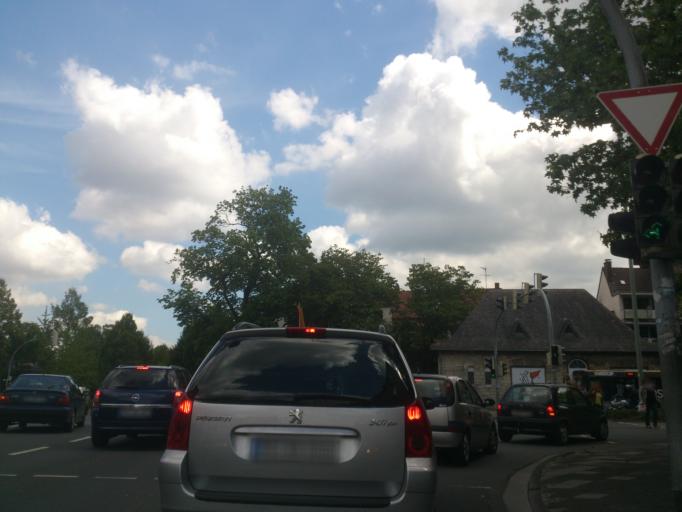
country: DE
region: North Rhine-Westphalia
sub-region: Regierungsbezirk Detmold
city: Paderborn
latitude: 51.7208
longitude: 8.7484
